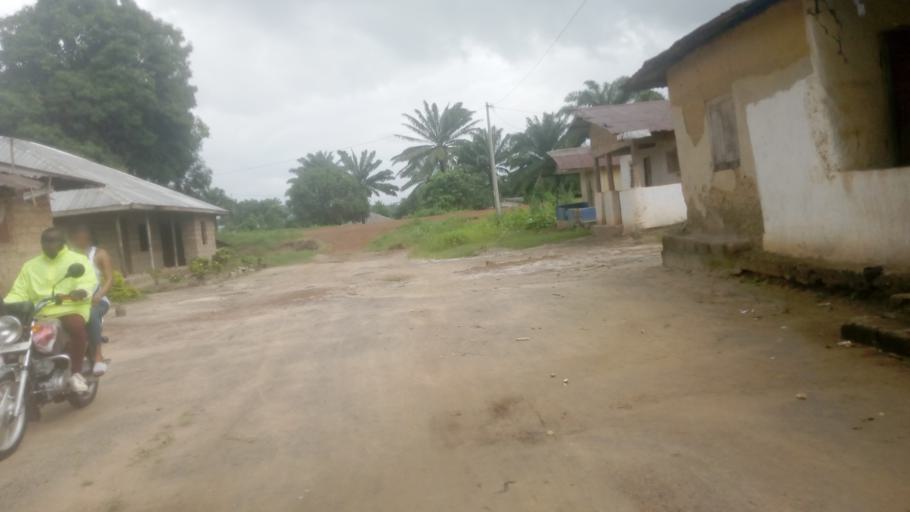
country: SL
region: Northern Province
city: Lunsar
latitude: 8.6828
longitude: -12.5417
